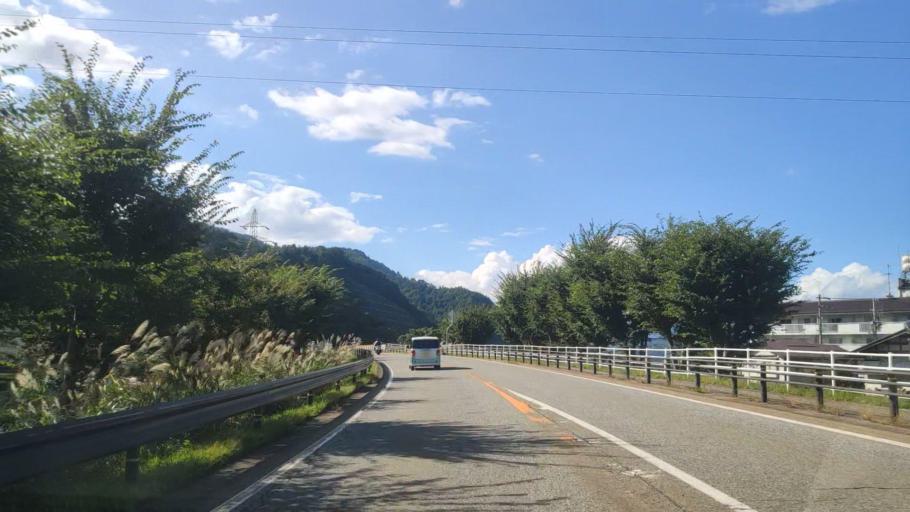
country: JP
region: Gifu
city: Takayama
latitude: 36.2292
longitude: 137.1841
